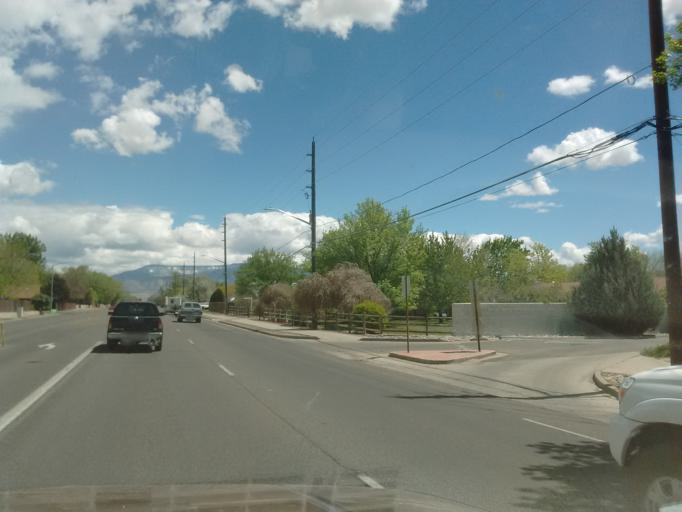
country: US
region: Colorado
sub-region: Mesa County
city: Fruitvale
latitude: 39.0918
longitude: -108.5128
